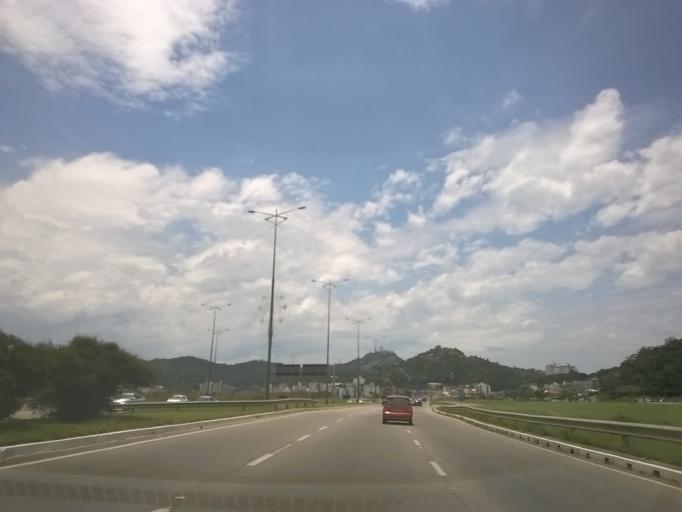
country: BR
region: Santa Catarina
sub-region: Florianopolis
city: Costeira do Pirajubae
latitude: -27.6220
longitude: -48.5278
